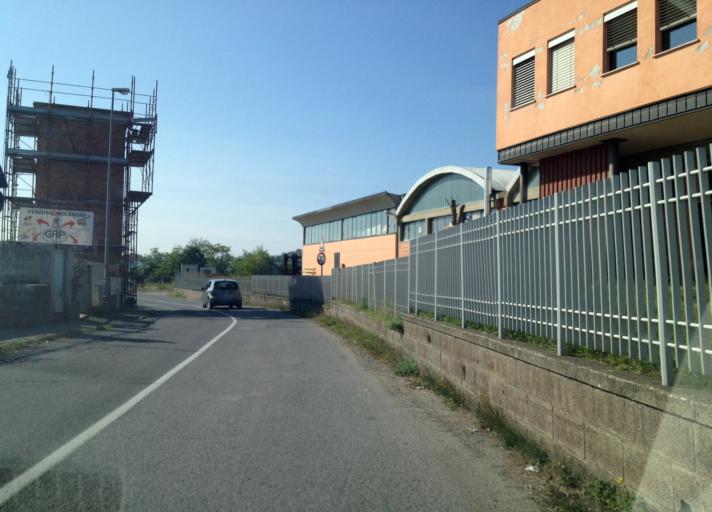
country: IT
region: Tuscany
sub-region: Provincia di Siena
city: Poggibonsi
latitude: 43.4809
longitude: 11.1337
